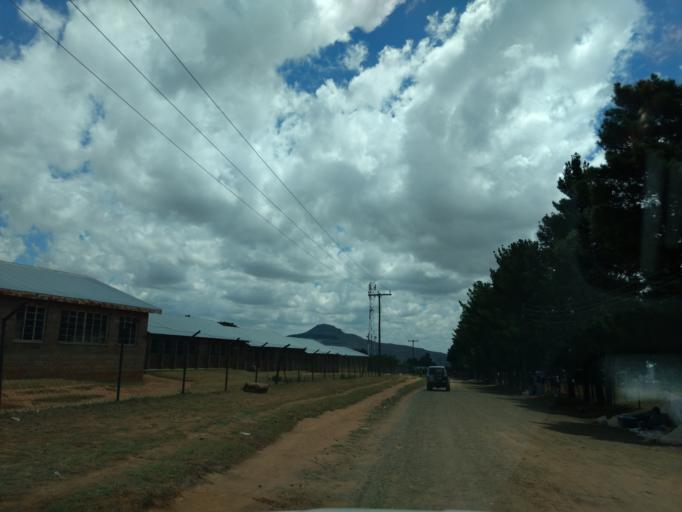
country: LS
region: Maseru
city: Maseru
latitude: -29.3724
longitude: 27.5093
